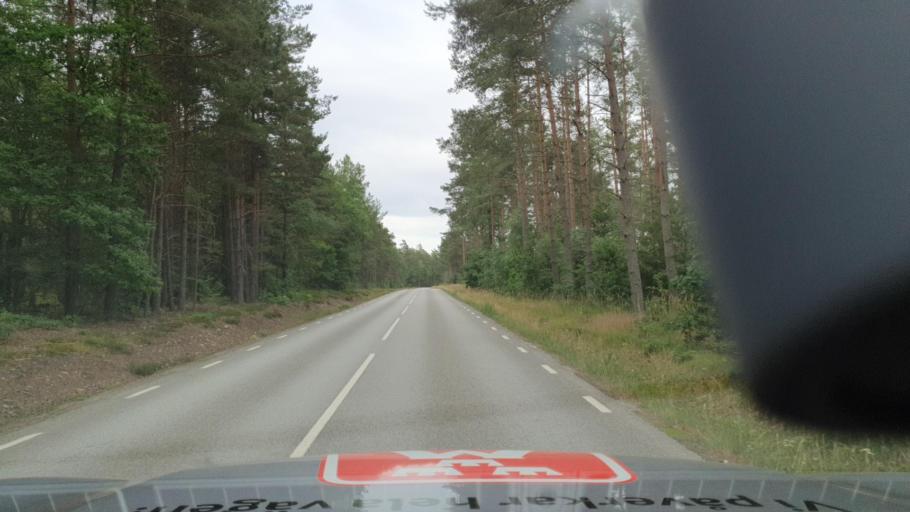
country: SE
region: Kalmar
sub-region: Kalmar Kommun
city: Trekanten
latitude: 56.6445
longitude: 16.0180
